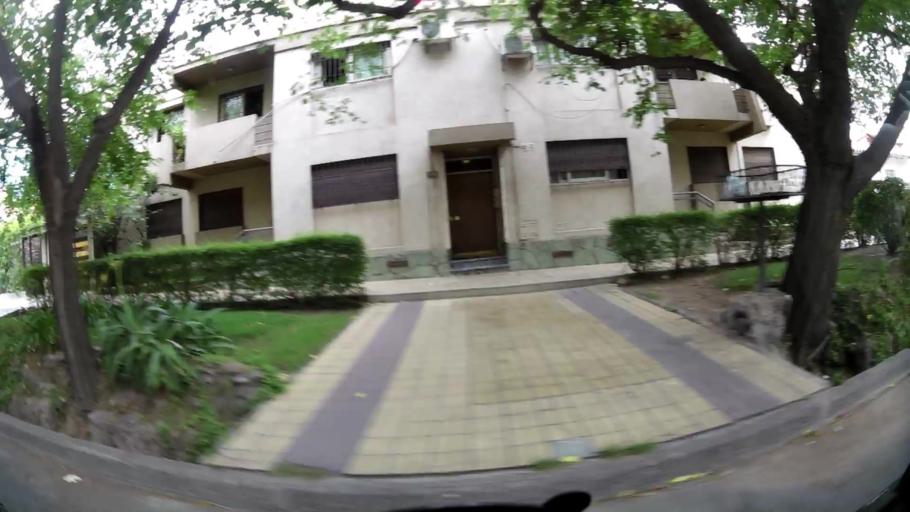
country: AR
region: Mendoza
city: Mendoza
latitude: -32.8744
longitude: -68.8558
